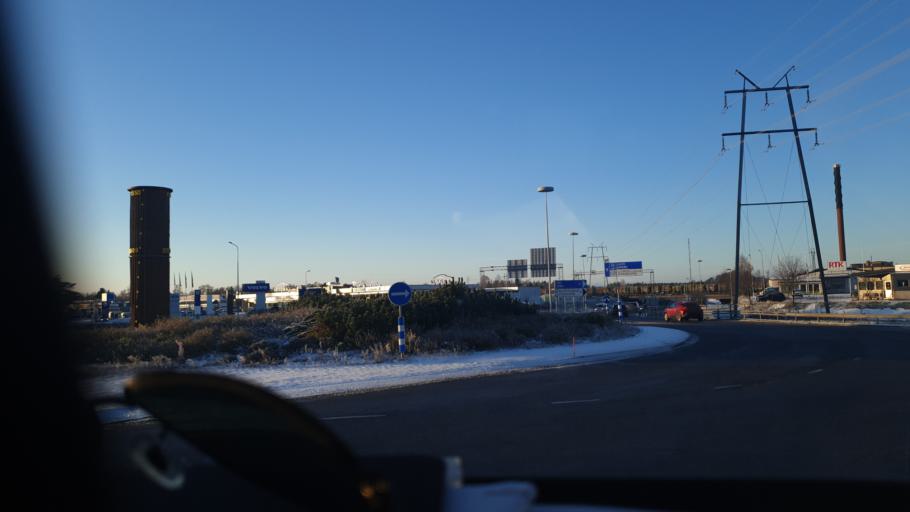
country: FI
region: Central Ostrobothnia
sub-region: Kokkola
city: Kokkola
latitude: 63.8309
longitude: 23.1219
